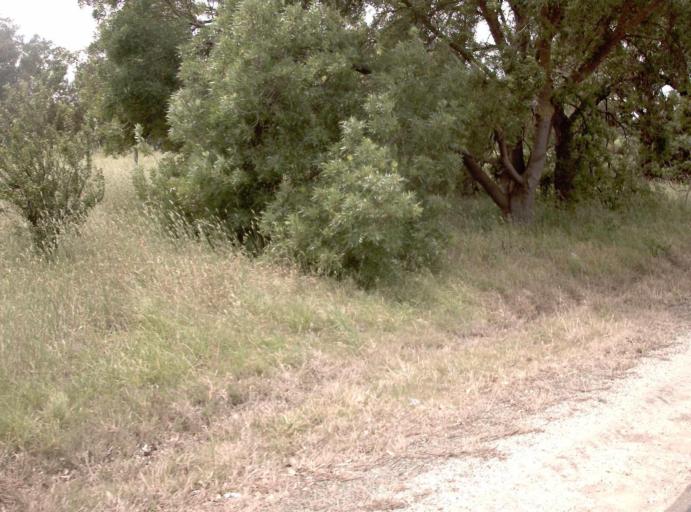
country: AU
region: Victoria
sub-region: Wellington
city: Sale
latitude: -37.9856
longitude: 146.9933
